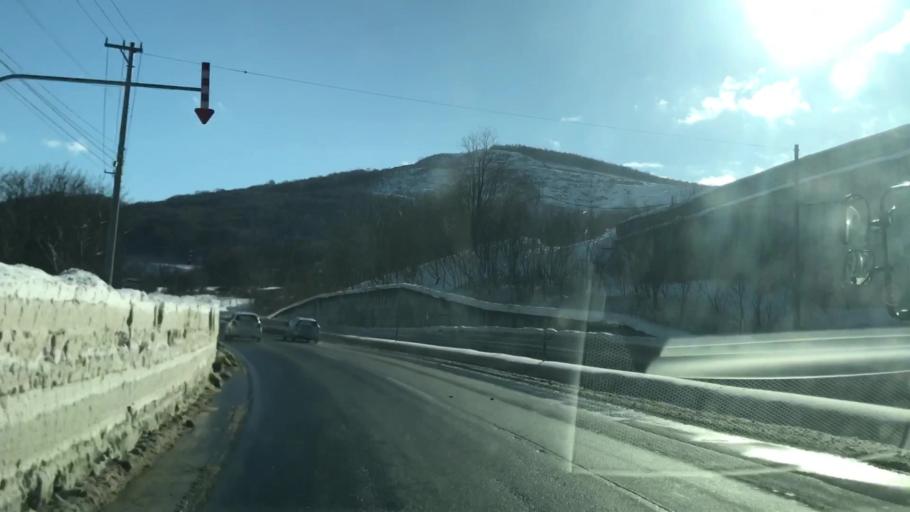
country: JP
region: Hokkaido
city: Otaru
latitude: 43.1729
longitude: 141.0701
